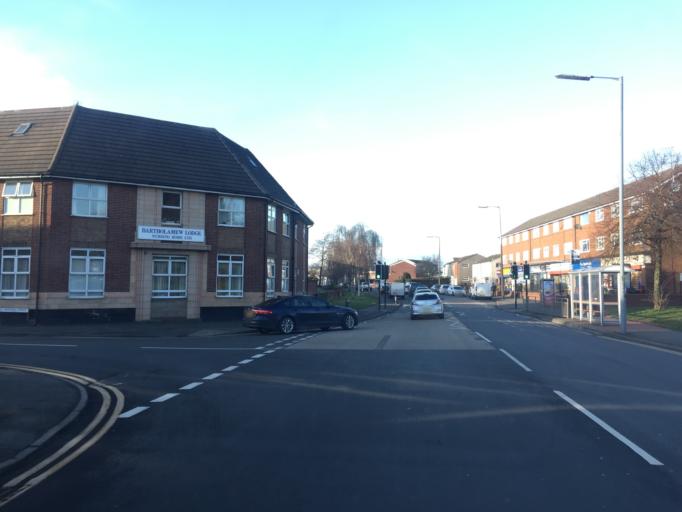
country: GB
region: England
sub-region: Sandwell
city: Wednesbury
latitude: 52.5543
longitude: -2.0229
